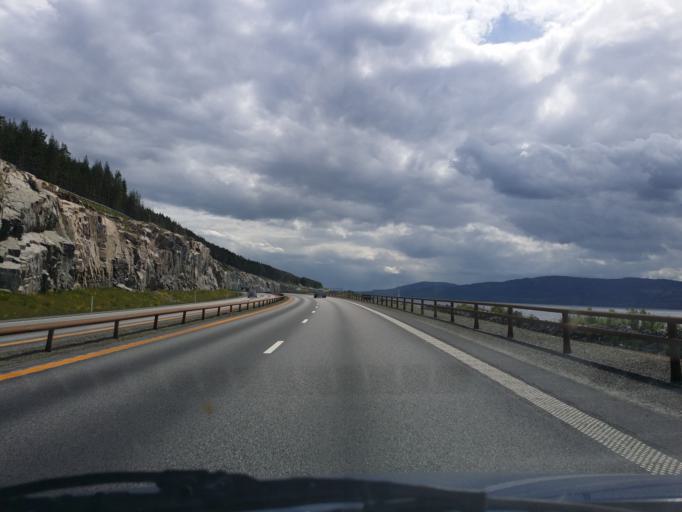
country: NO
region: Hedmark
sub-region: Stange
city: Stange
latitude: 60.5497
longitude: 11.2472
